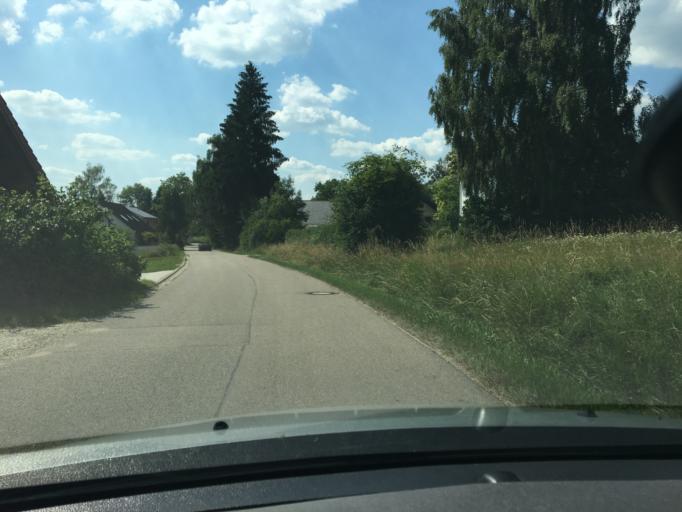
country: DE
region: Bavaria
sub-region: Lower Bavaria
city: Vilsheim
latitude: 48.4502
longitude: 12.0941
